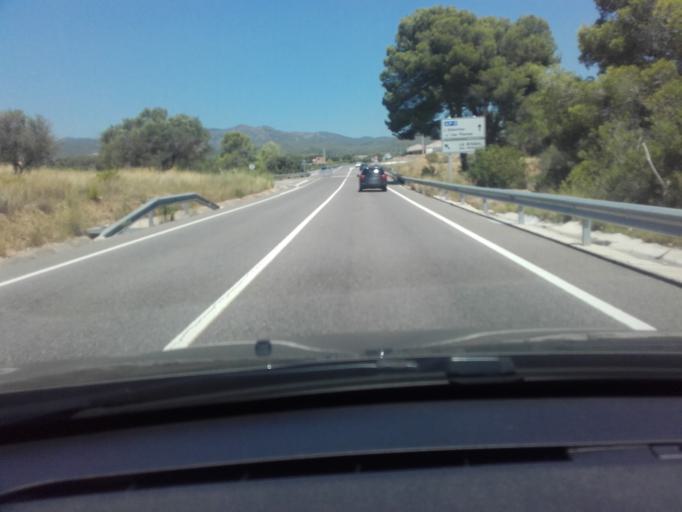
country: ES
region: Catalonia
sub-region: Provincia de Tarragona
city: Albinyana
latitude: 41.2631
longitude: 1.4977
